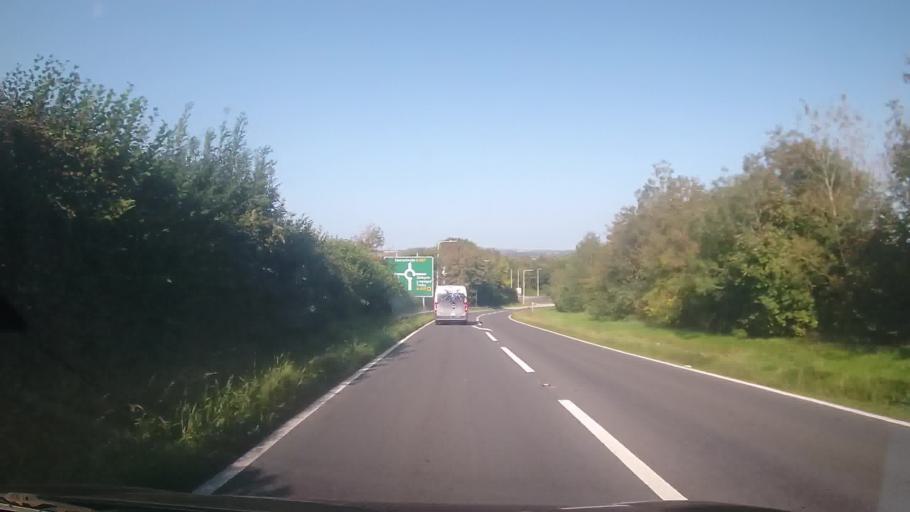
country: GB
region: Wales
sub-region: County of Ceredigion
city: Cardigan
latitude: 52.0746
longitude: -4.6575
